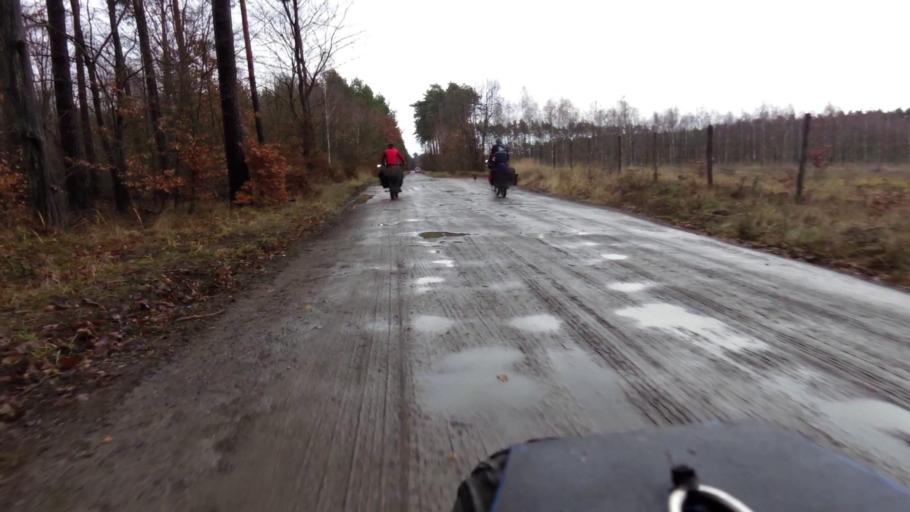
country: PL
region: Lubusz
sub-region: Powiat gorzowski
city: Witnica
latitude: 52.7023
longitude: 14.8335
